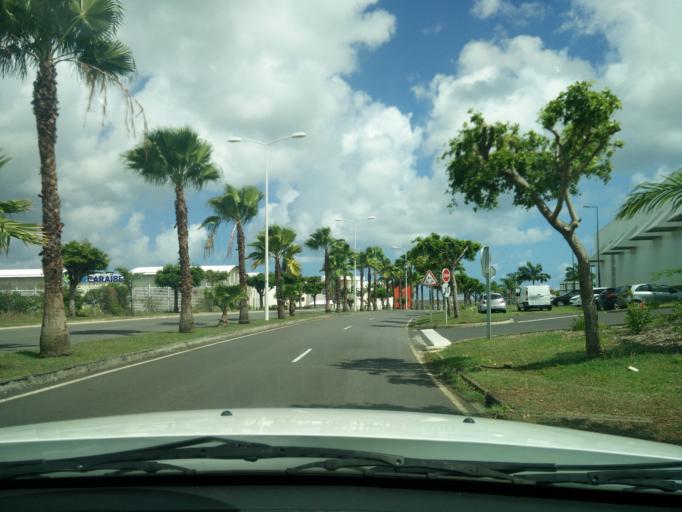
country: GP
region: Guadeloupe
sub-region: Guadeloupe
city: Les Abymes
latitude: 16.2666
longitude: -61.5170
